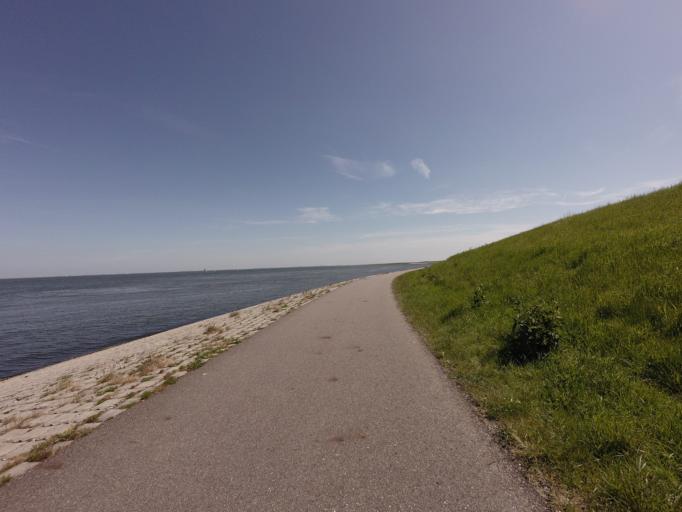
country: NL
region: Zeeland
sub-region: Gemeente Noord-Beveland
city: Kamperland
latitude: 51.6017
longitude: 3.7806
